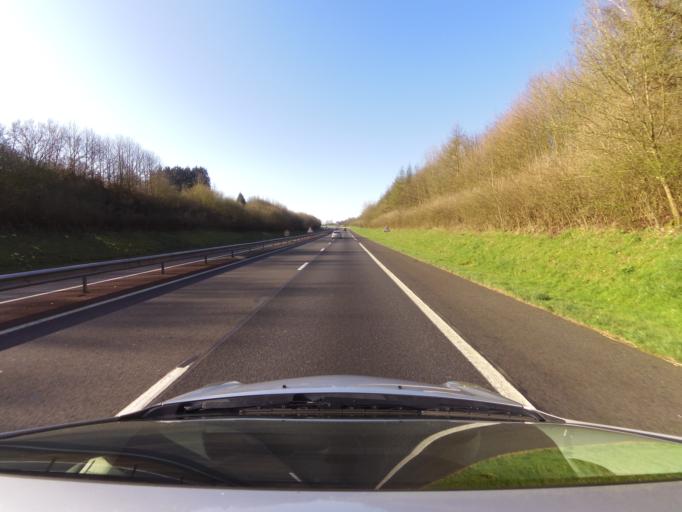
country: FR
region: Lower Normandy
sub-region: Departement de la Manche
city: Villedieu-les-Poeles
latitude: 48.8022
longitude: -1.2617
